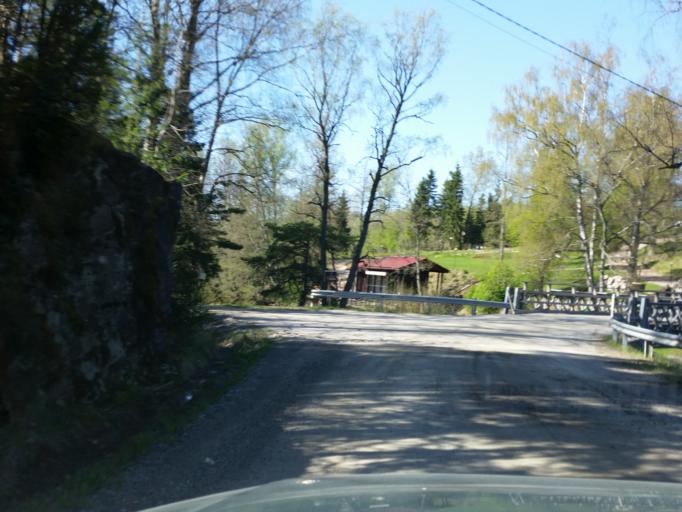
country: FI
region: Uusimaa
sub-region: Helsinki
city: Karjalohja
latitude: 60.1408
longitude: 23.7537
